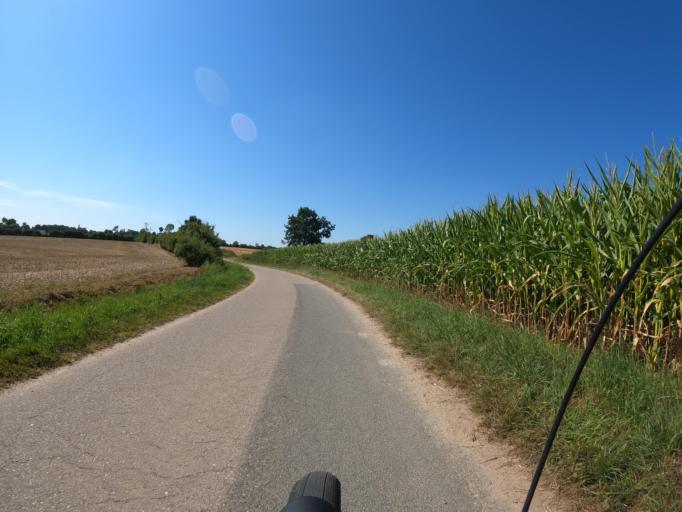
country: DE
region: Schleswig-Holstein
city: Steinberg
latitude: 54.7616
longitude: 9.7794
